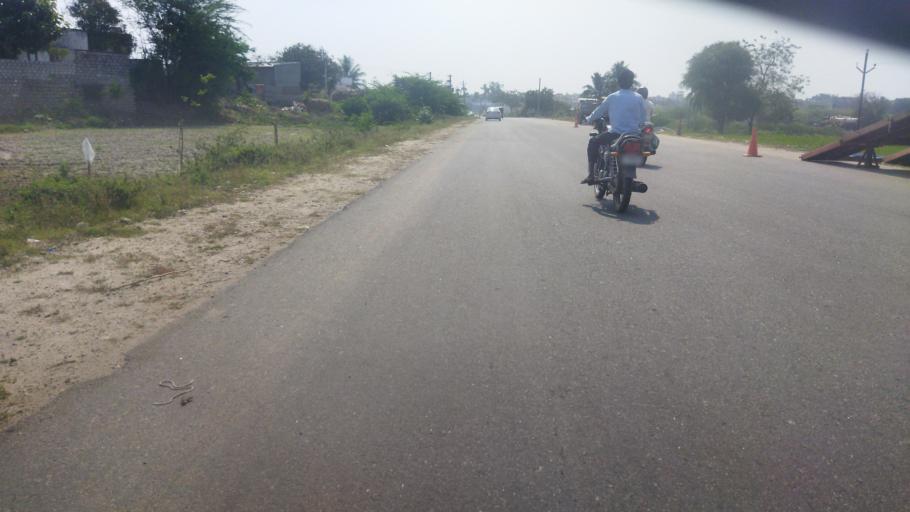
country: IN
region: Telangana
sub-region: Nalgonda
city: Nalgonda
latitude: 17.0772
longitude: 79.2837
